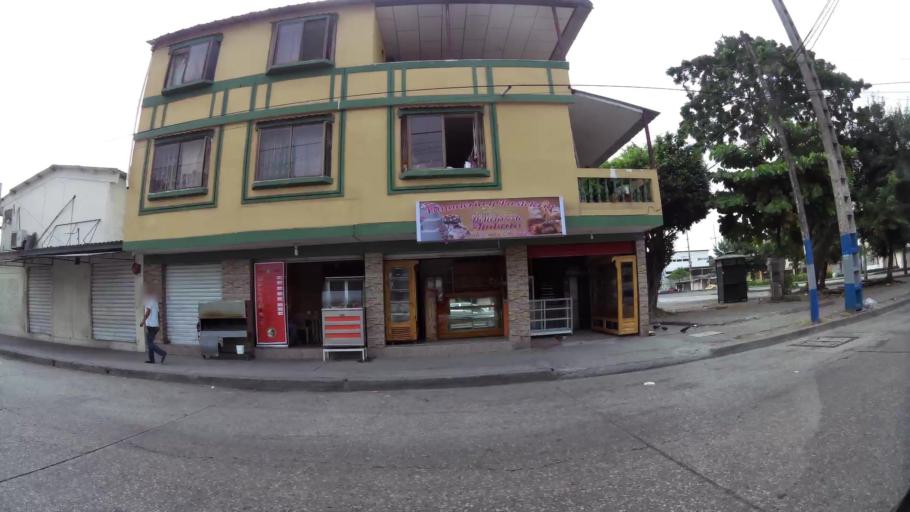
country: EC
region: Guayas
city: Eloy Alfaro
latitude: -2.1351
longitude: -79.8876
